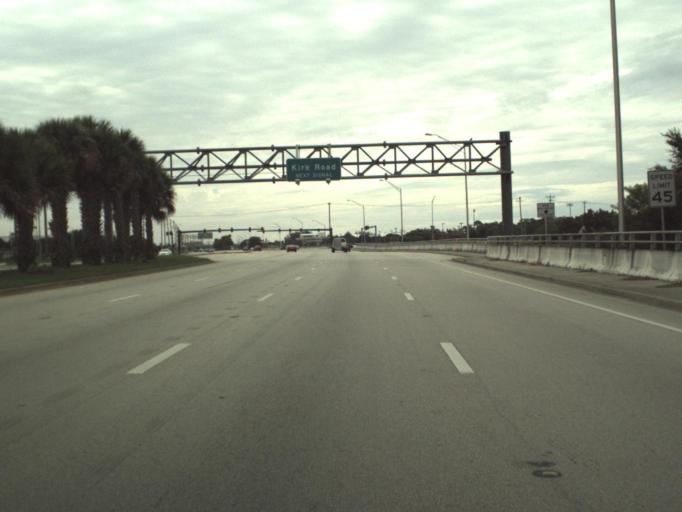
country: US
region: Florida
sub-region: Palm Beach County
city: Royal Palm Estates
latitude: 26.6776
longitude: -80.1069
